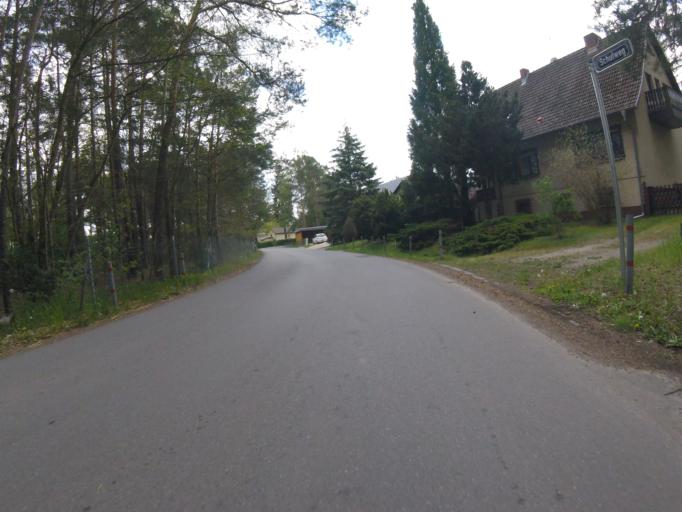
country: DE
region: Brandenburg
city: Teupitz
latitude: 52.1189
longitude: 13.6223
